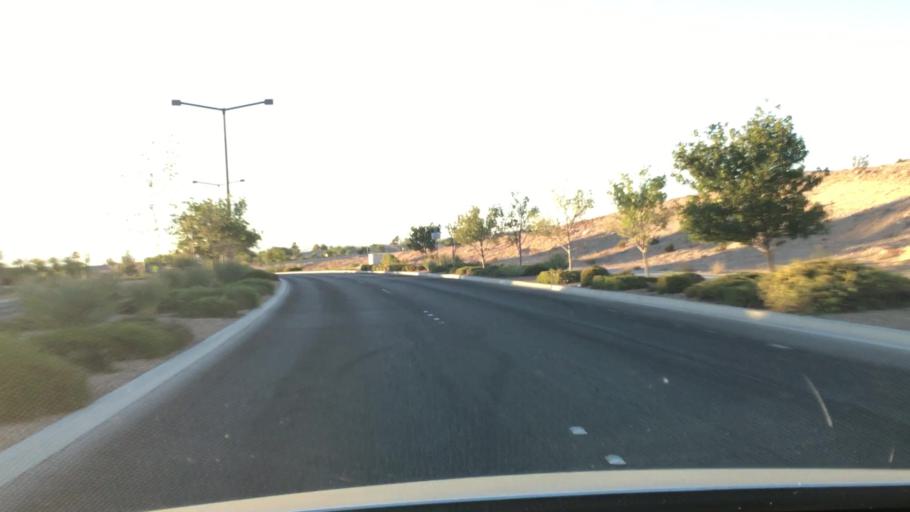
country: US
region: Nevada
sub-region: Clark County
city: Summerlin South
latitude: 36.1019
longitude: -115.3272
